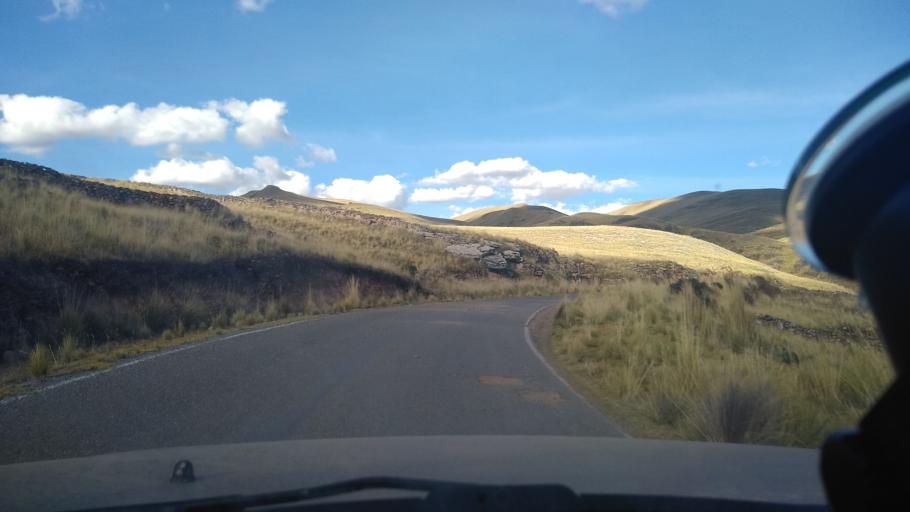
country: PE
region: Cusco
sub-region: Provincia de Canas
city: Cahuanuyo
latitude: -14.3420
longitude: -71.4481
